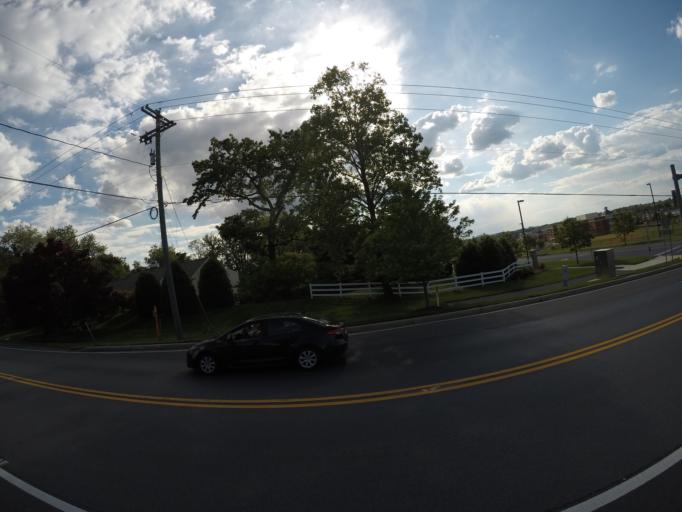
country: US
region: Maryland
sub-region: Montgomery County
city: Clarksburg
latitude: 39.2293
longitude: -77.2353
